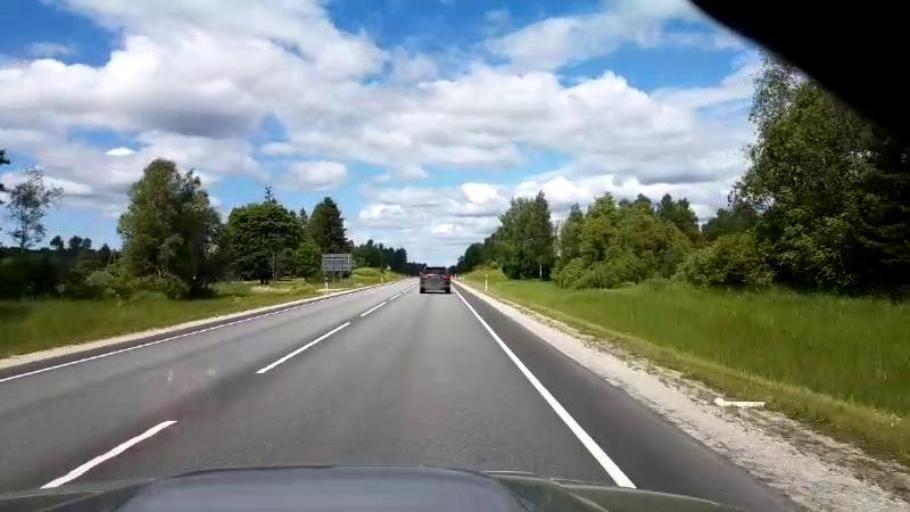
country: EE
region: Harju
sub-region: Nissi vald
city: Riisipere
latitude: 59.0520
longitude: 24.4455
